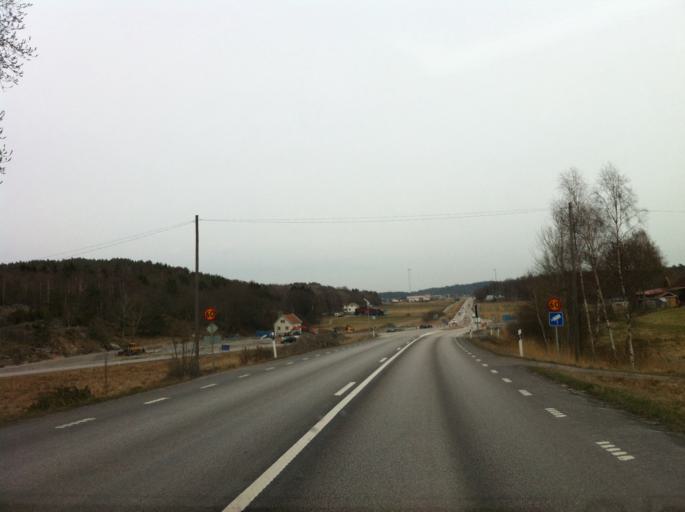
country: SE
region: Vaestra Goetaland
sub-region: Tjorns Kommun
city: Myggenas
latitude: 58.0082
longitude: 11.6733
